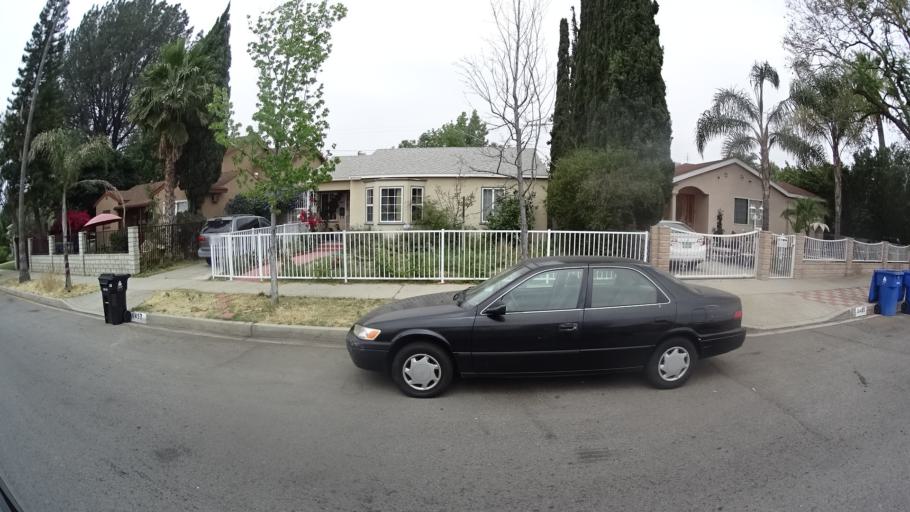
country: US
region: California
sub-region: Los Angeles County
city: North Hollywood
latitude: 34.1884
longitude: -118.4091
